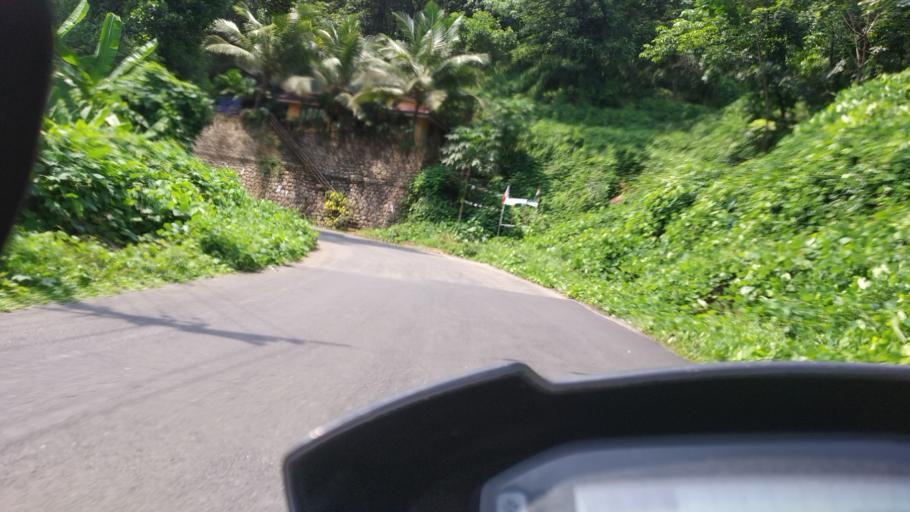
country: IN
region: Kerala
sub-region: Kottayam
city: Erattupetta
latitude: 9.6900
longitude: 76.8450
